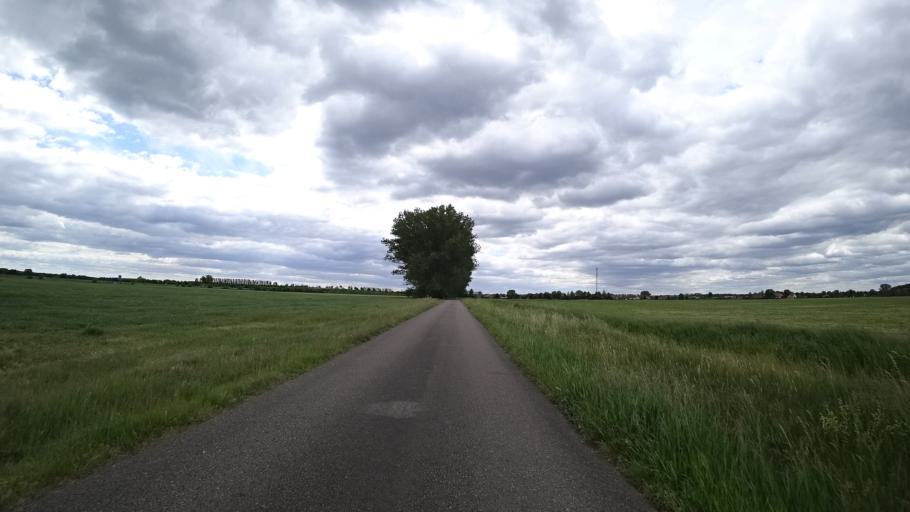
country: DE
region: Brandenburg
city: Trebbin
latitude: 52.1827
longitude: 13.2452
